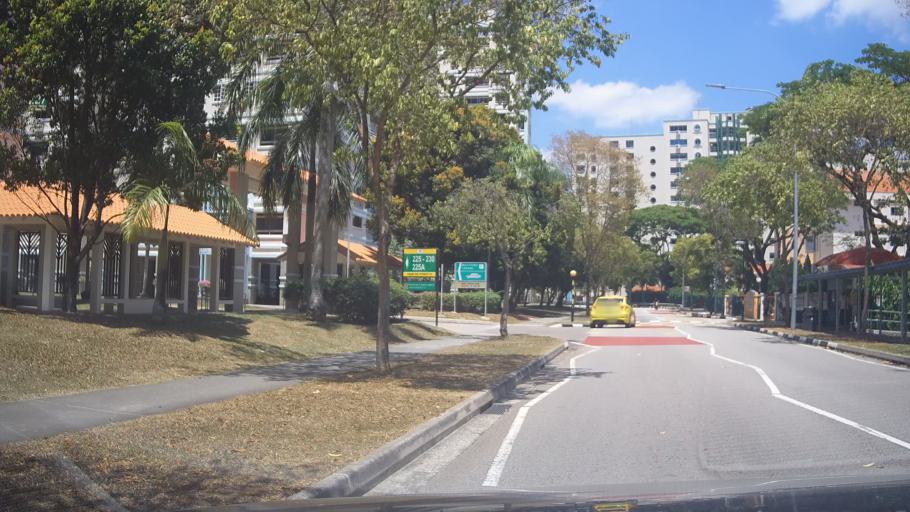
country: MY
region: Johor
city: Kampung Pasir Gudang Baru
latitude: 1.3714
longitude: 103.9621
